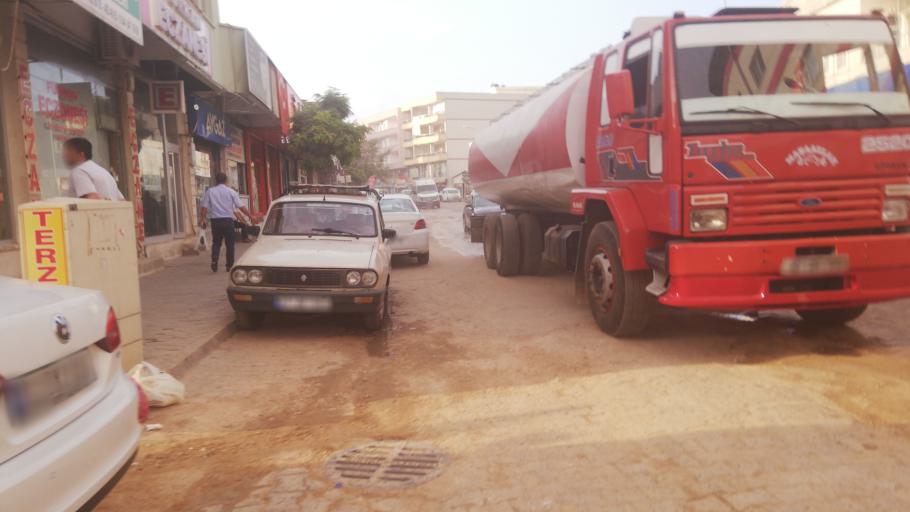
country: TR
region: Mardin
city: Midyat
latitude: 37.4262
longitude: 41.3394
